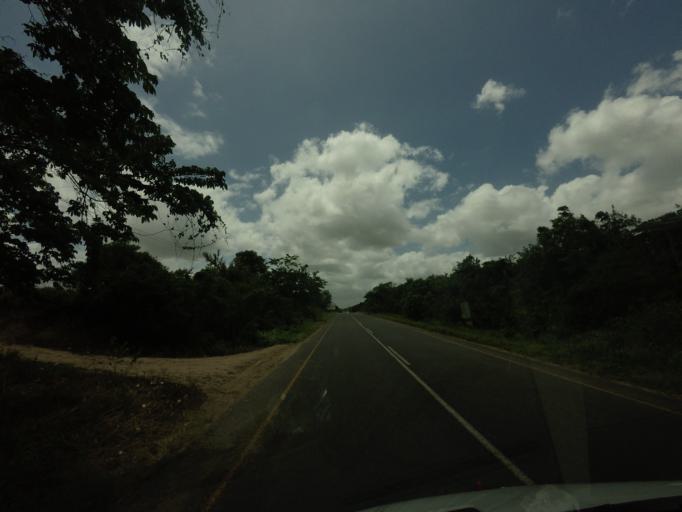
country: ZA
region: KwaZulu-Natal
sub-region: uMkhanyakude District Municipality
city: Mtubatuba
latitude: -28.3824
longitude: 32.3570
